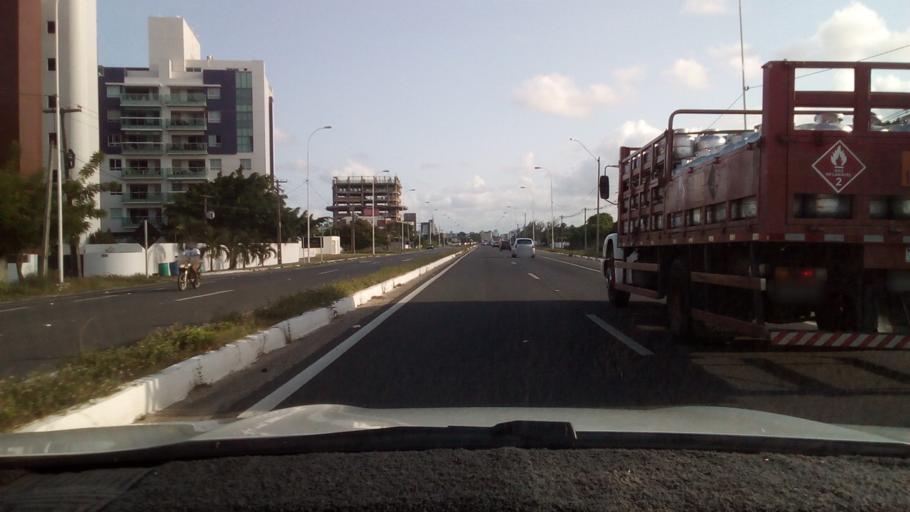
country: BR
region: Paraiba
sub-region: Cabedelo
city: Cabedelo
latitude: -6.9964
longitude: -34.8283
